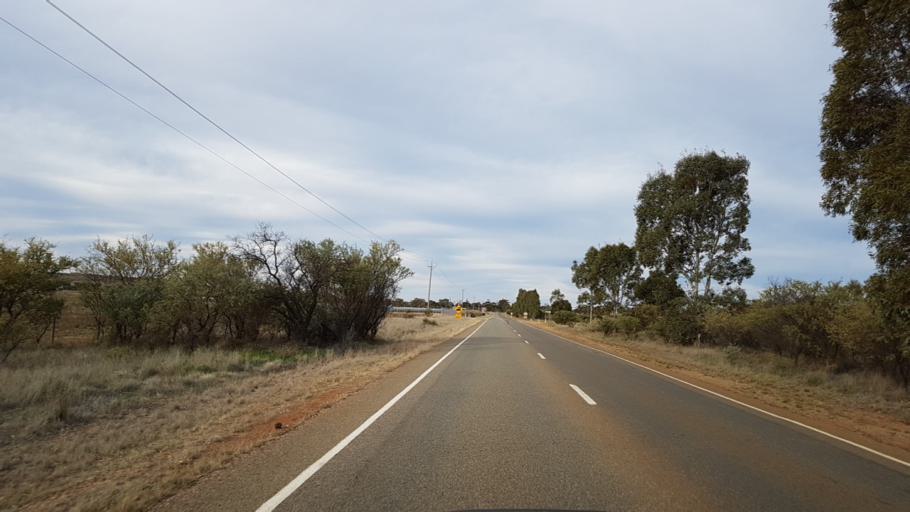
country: AU
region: South Australia
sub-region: Peterborough
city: Peterborough
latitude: -32.9820
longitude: 138.8116
